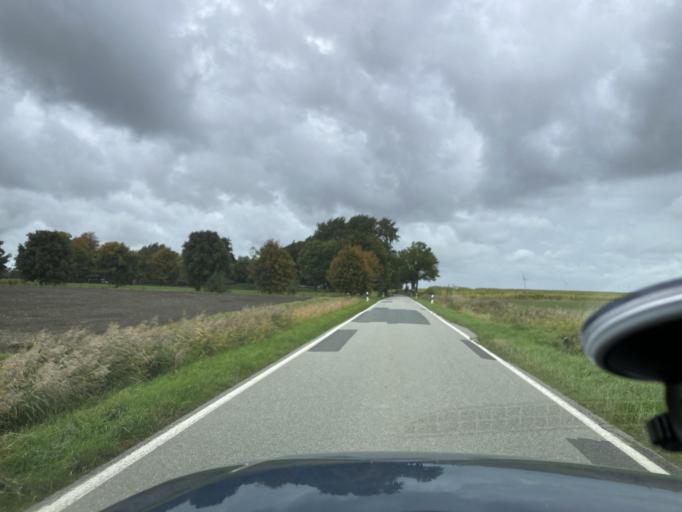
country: DE
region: Schleswig-Holstein
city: Norderwohrden
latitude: 54.2029
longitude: 8.9979
